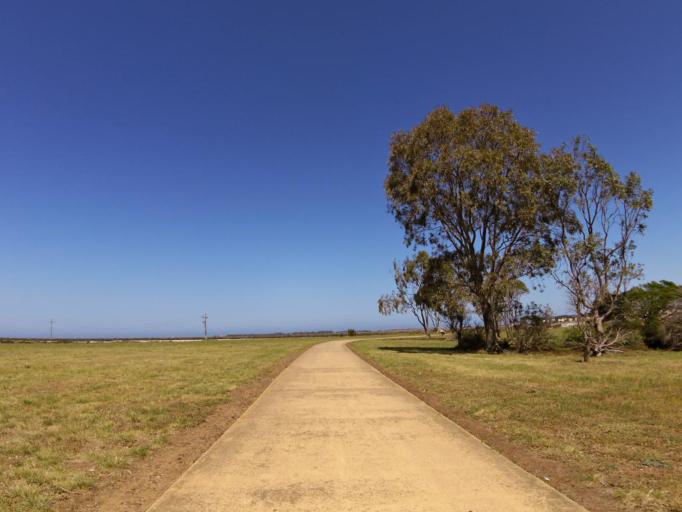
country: AU
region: Victoria
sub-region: Hobsons Bay
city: Altona Meadows
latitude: -37.8957
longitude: 144.7817
